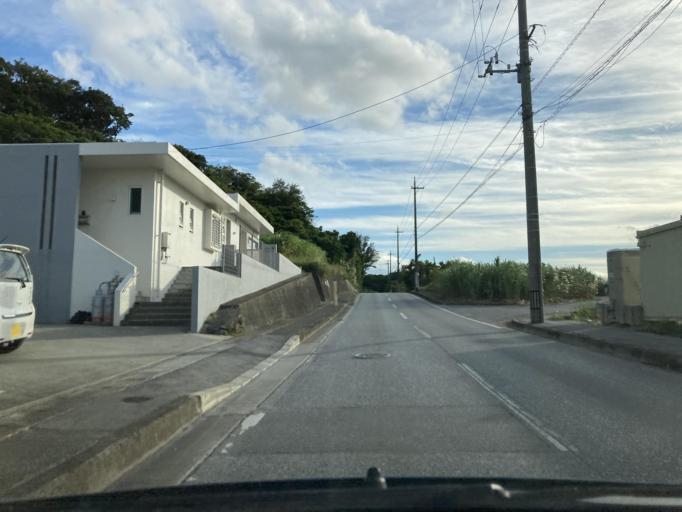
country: JP
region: Okinawa
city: Tomigusuku
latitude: 26.1487
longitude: 127.7447
